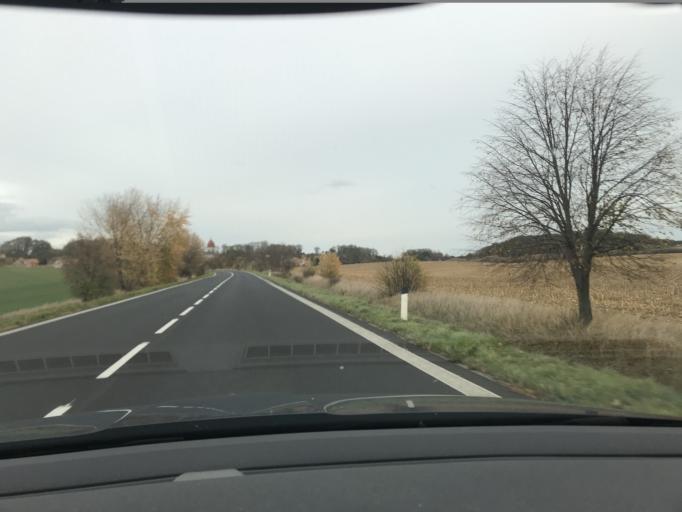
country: CZ
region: Ustecky
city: Budyne nad Ohri
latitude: 50.4100
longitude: 14.1721
